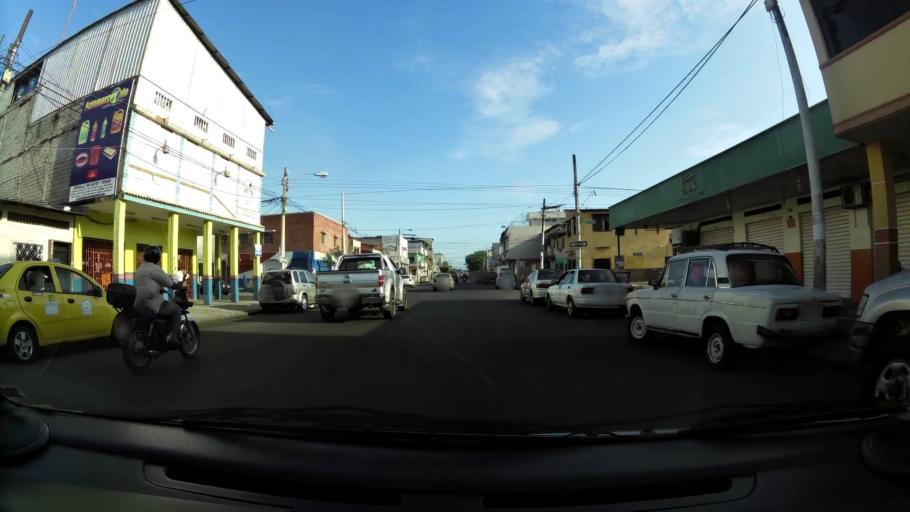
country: EC
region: Guayas
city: Guayaquil
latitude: -2.2125
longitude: -79.9016
